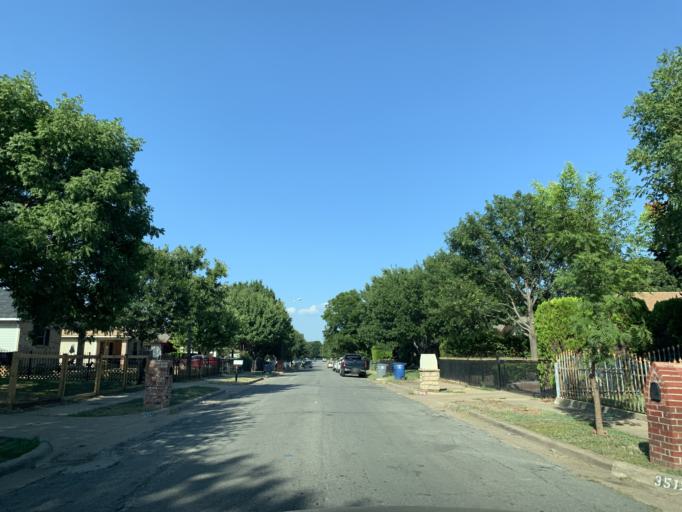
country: US
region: Texas
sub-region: Dallas County
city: Hutchins
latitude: 32.6670
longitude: -96.7653
